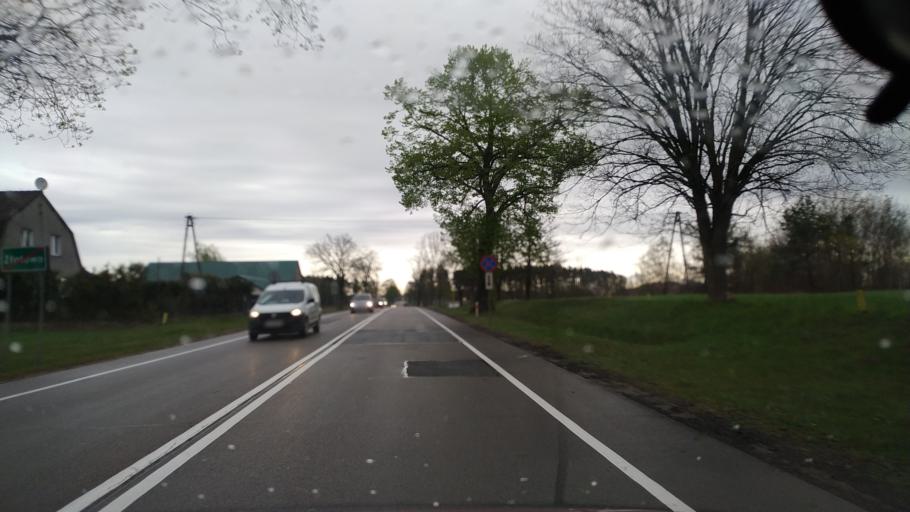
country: PL
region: Pomeranian Voivodeship
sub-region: Powiat chojnicki
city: Czersk
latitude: 53.8066
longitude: 18.0182
